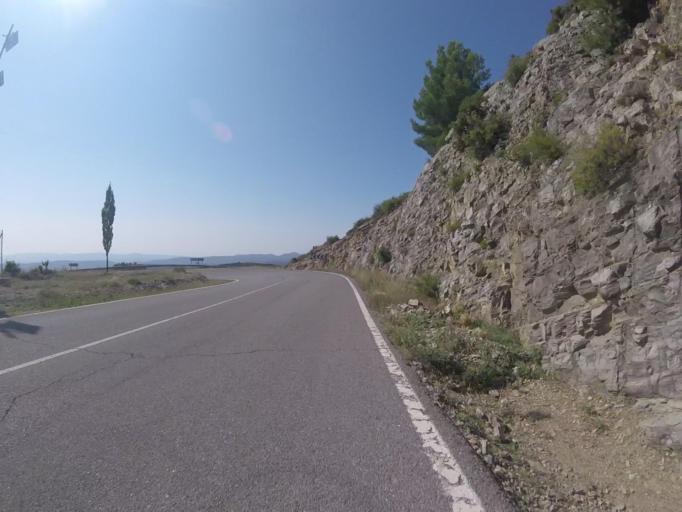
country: ES
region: Valencia
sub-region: Provincia de Castello
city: Benafigos
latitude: 40.2639
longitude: -0.2326
